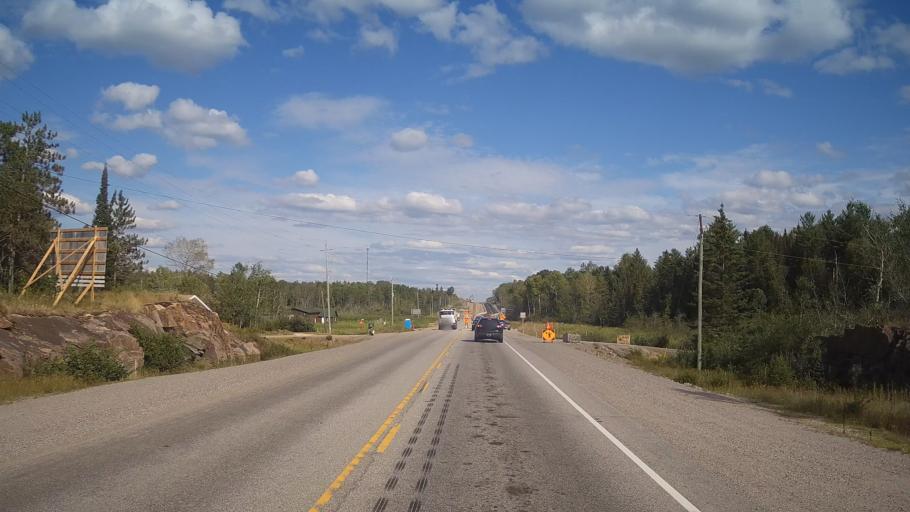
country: CA
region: Ontario
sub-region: Nipissing District
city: North Bay
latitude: 46.2843
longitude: -79.3182
